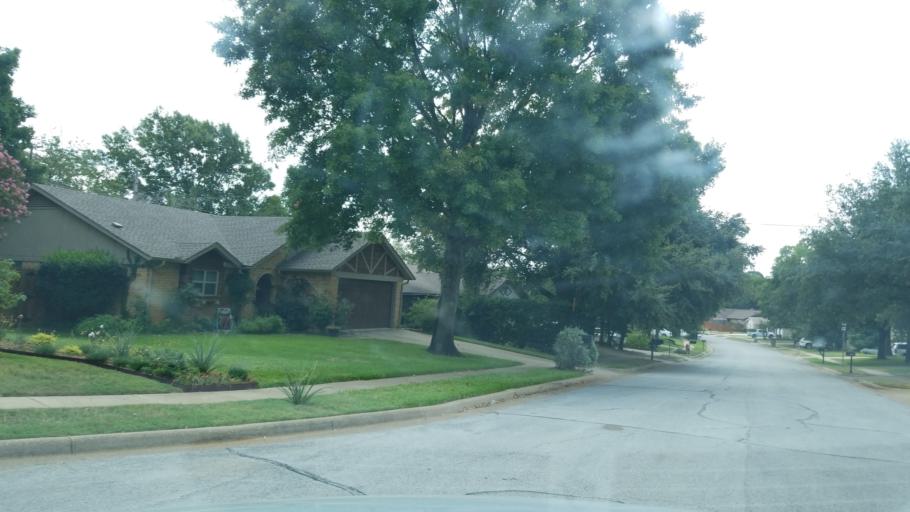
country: US
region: Texas
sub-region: Tarrant County
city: Euless
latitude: 32.8469
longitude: -97.0972
